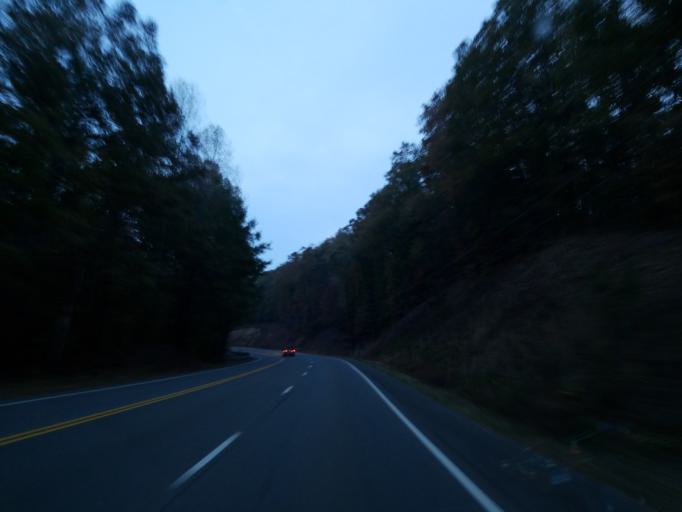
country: US
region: Georgia
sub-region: Pickens County
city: Jasper
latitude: 34.5057
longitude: -84.4883
